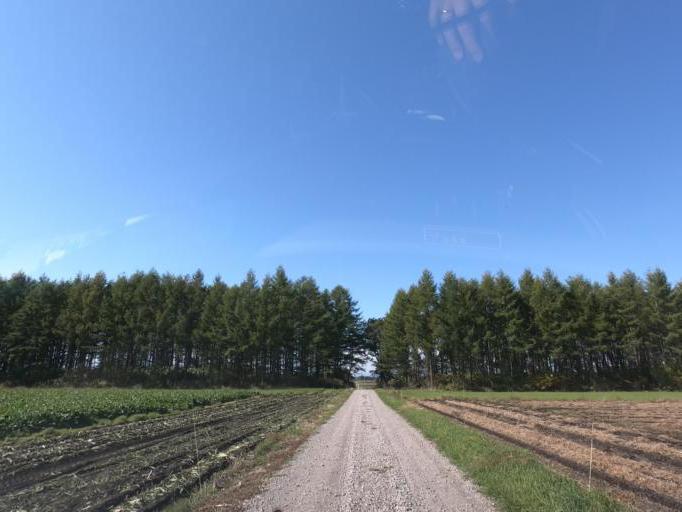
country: JP
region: Hokkaido
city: Otofuke
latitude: 43.0711
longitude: 143.2642
